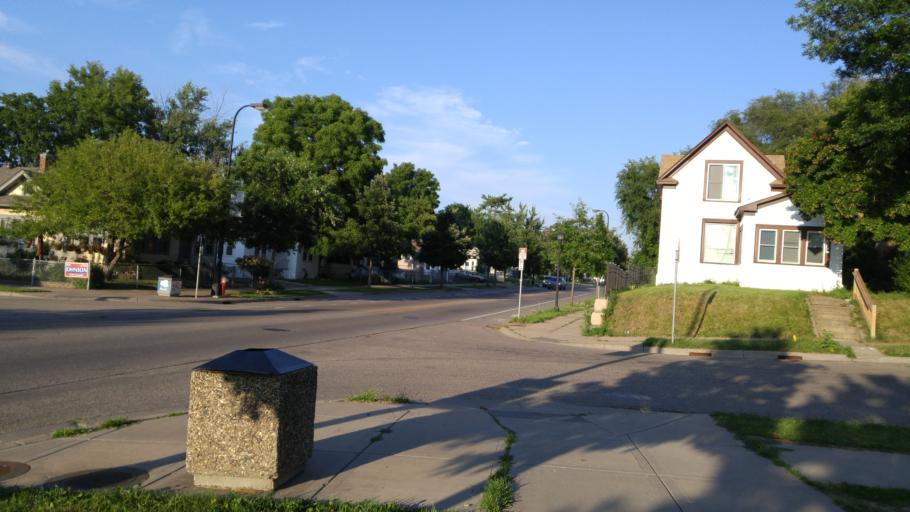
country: US
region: Minnesota
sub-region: Anoka County
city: Columbia Heights
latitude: 45.0130
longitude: -93.2932
